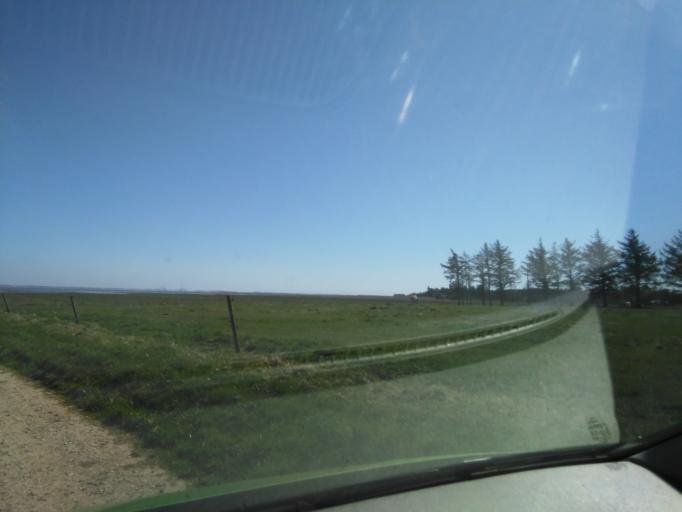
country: DK
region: South Denmark
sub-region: Varde Kommune
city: Oksbol
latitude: 55.5535
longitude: 8.2324
